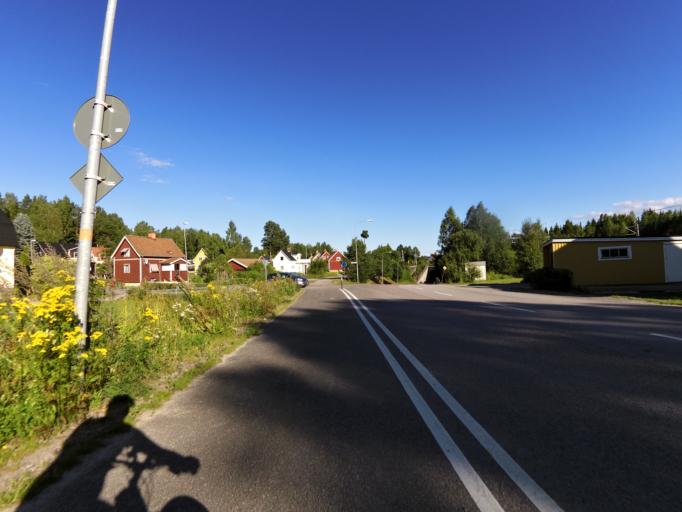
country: SE
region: Gaevleborg
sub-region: Hofors Kommun
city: Hofors
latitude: 60.5690
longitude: 16.2747
